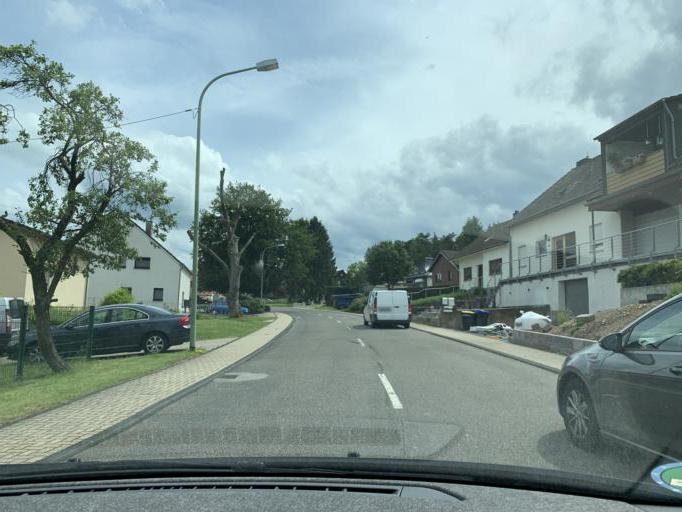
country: DE
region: North Rhine-Westphalia
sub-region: Regierungsbezirk Koln
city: Hurtgenwald
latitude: 50.6764
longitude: 6.4081
